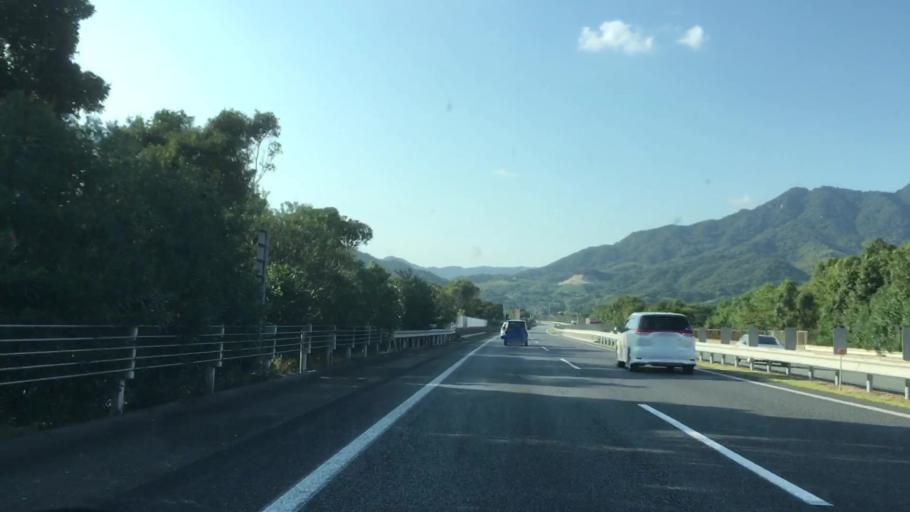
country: JP
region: Yamaguchi
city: Hofu
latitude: 34.0630
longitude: 131.6075
